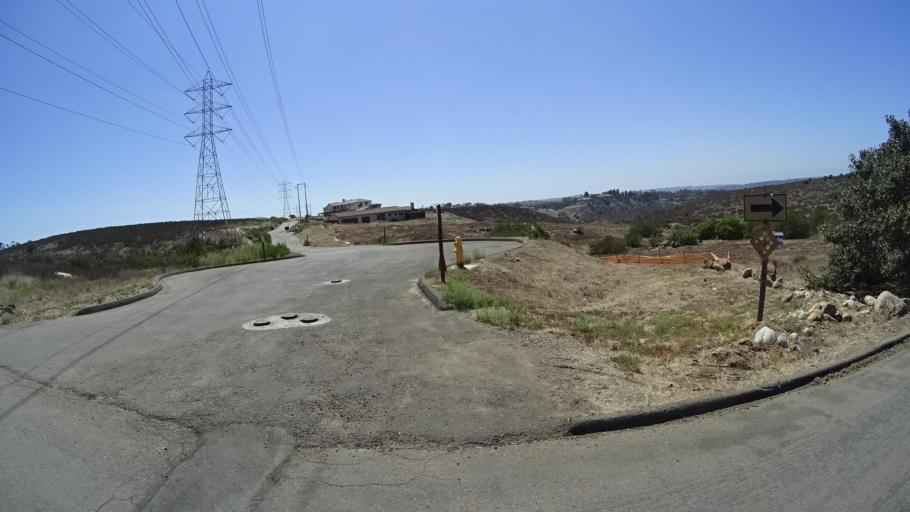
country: US
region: California
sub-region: San Diego County
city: Fairbanks Ranch
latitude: 33.0183
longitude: -117.1692
